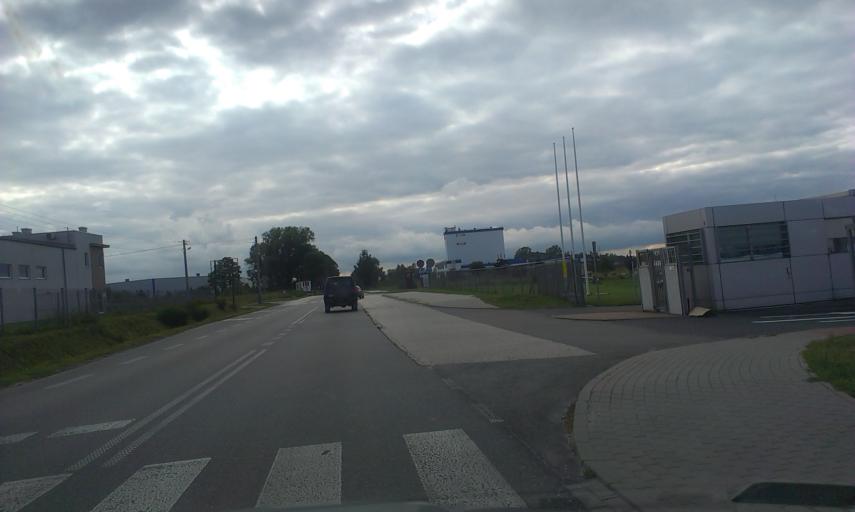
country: PL
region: Masovian Voivodeship
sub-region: Powiat zyrardowski
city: Mszczonow
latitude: 51.9728
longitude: 20.5570
